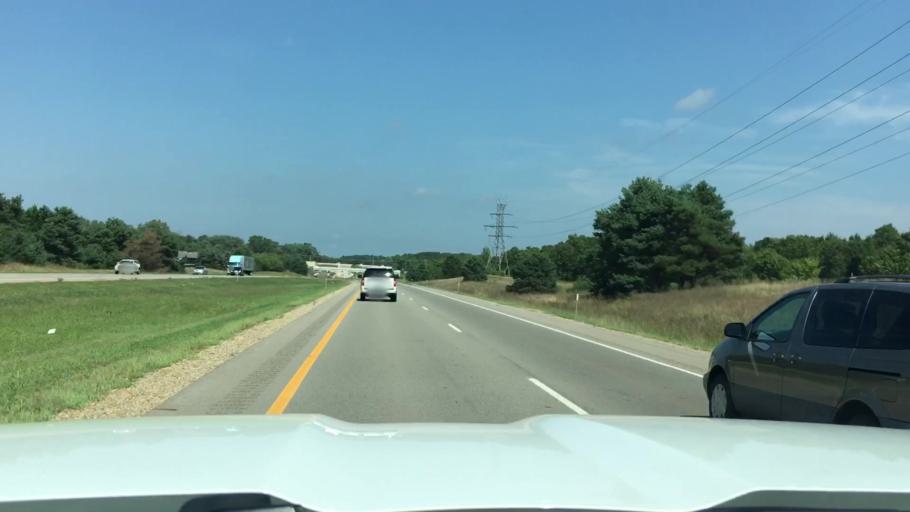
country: US
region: Michigan
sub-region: Kalamazoo County
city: Portage
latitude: 42.2242
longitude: -85.6401
